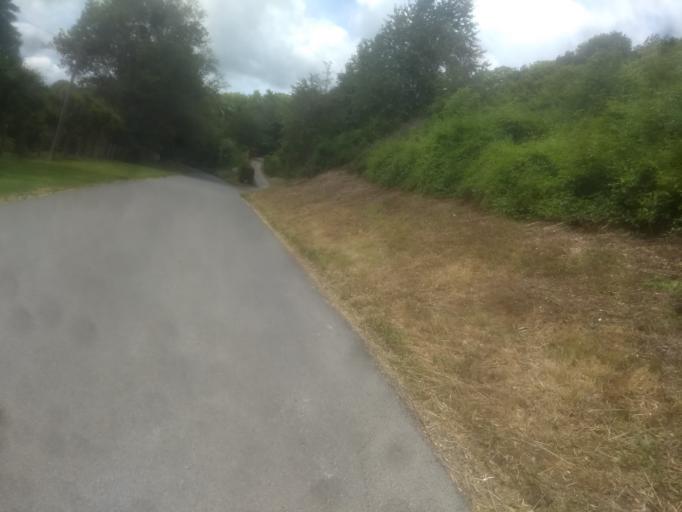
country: FR
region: Nord-Pas-de-Calais
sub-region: Departement du Pas-de-Calais
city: Mont-Saint-Eloi
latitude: 50.3401
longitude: 2.6906
